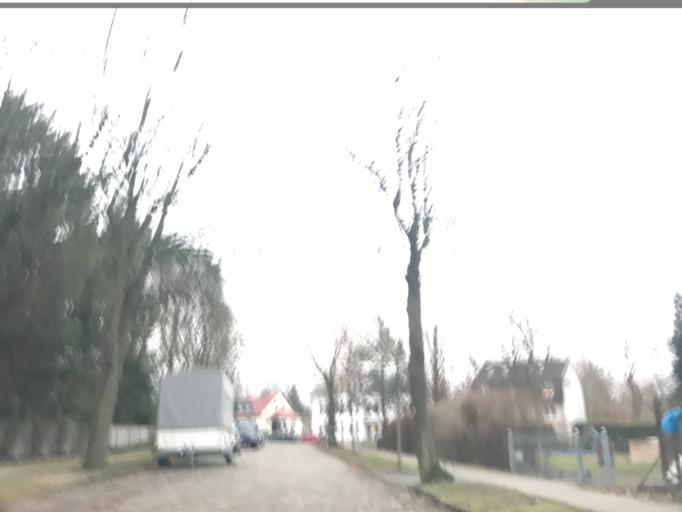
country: DE
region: Brandenburg
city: Falkensee
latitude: 52.5746
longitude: 13.1080
